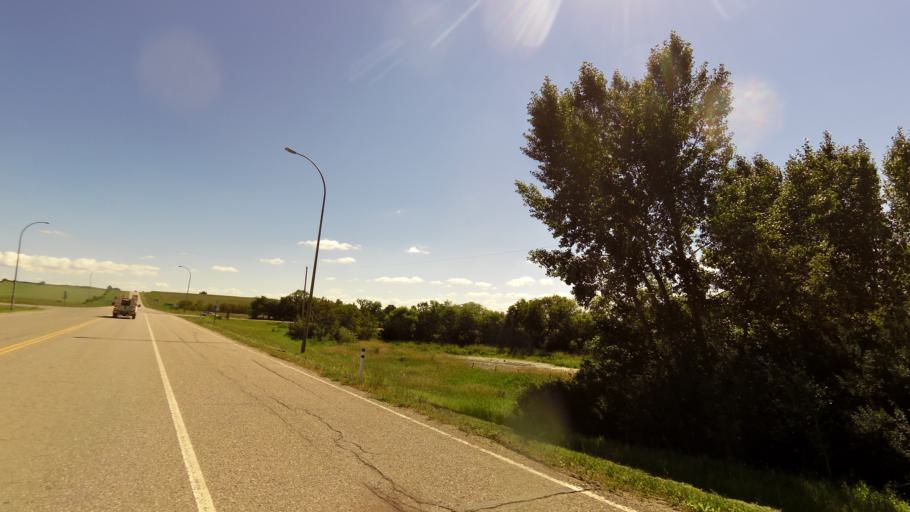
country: CA
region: Saskatchewan
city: Lloydminster
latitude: 52.8416
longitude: -110.0189
